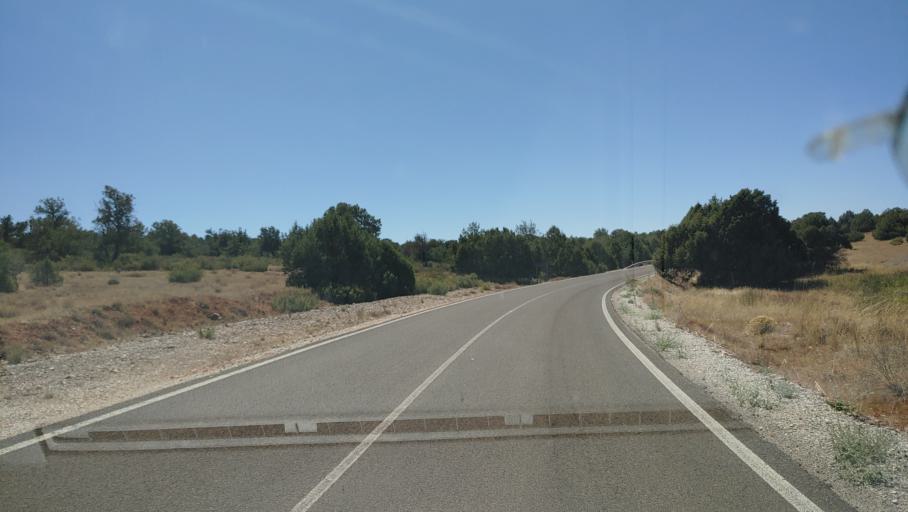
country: ES
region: Castille-La Mancha
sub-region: Provincia de Albacete
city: Ossa de Montiel
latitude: 38.8702
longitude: -2.7893
